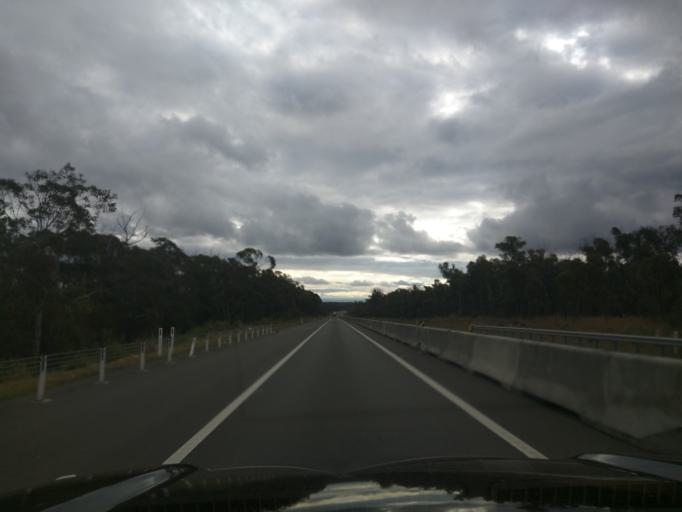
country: AU
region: New South Wales
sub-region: Wollongong
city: Mount Keira
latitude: -34.3384
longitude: 150.7905
